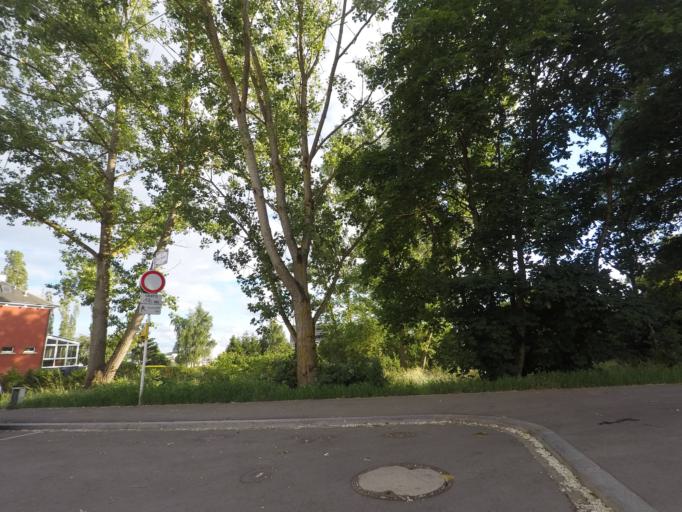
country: LU
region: Luxembourg
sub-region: Canton de Luxembourg
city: Luxembourg
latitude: 49.5895
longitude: 6.1285
